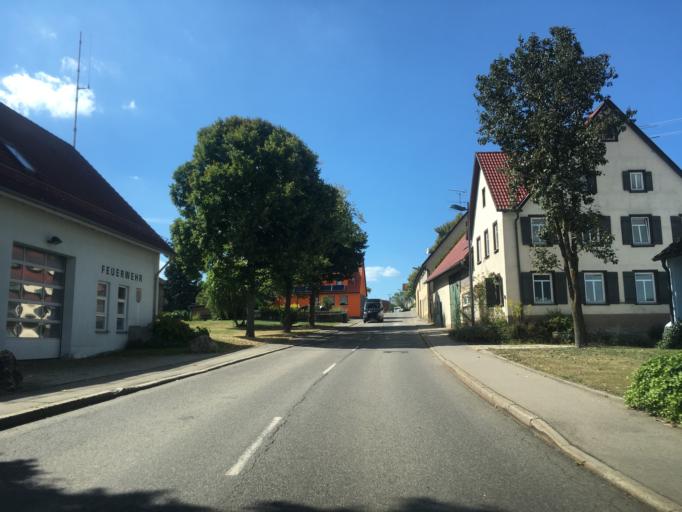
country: DE
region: Baden-Wuerttemberg
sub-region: Tuebingen Region
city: Gomadingen
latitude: 48.3493
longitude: 9.4261
